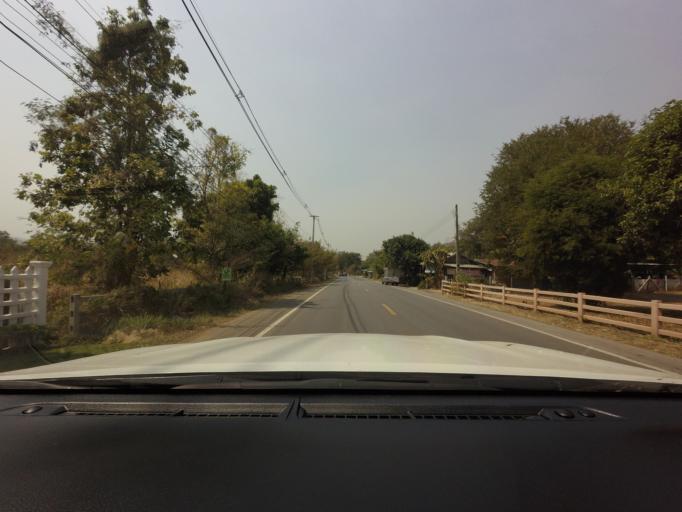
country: TH
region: Sara Buri
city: Muak Lek
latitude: 14.5900
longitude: 101.2323
